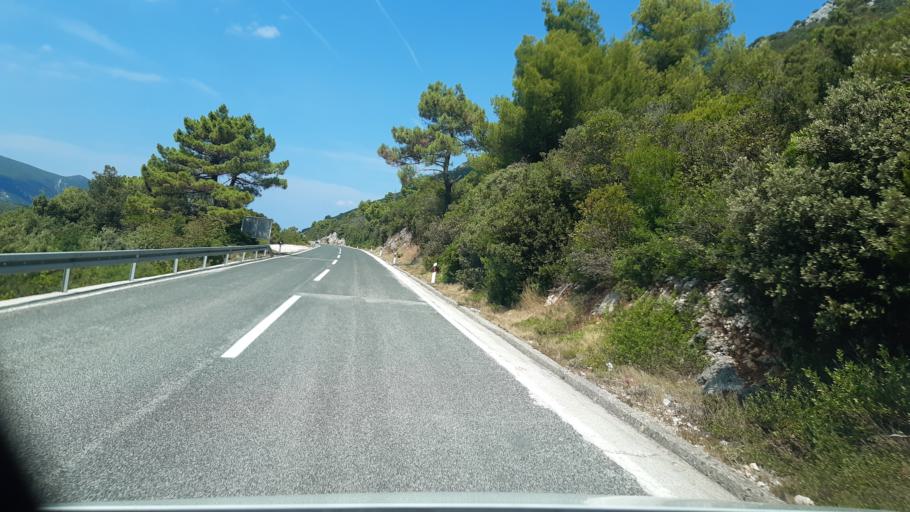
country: HR
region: Dubrovacko-Neretvanska
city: Ston
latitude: 42.8714
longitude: 17.6852
